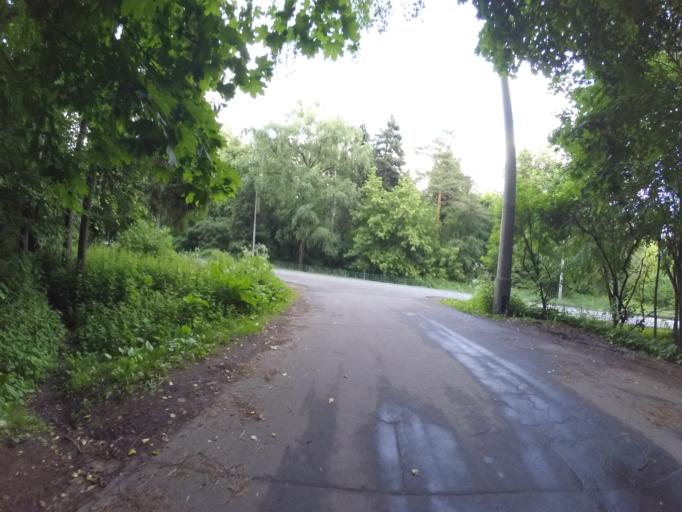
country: RU
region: Moskovskaya
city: Kastanayevo
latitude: 55.7270
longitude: 37.4922
